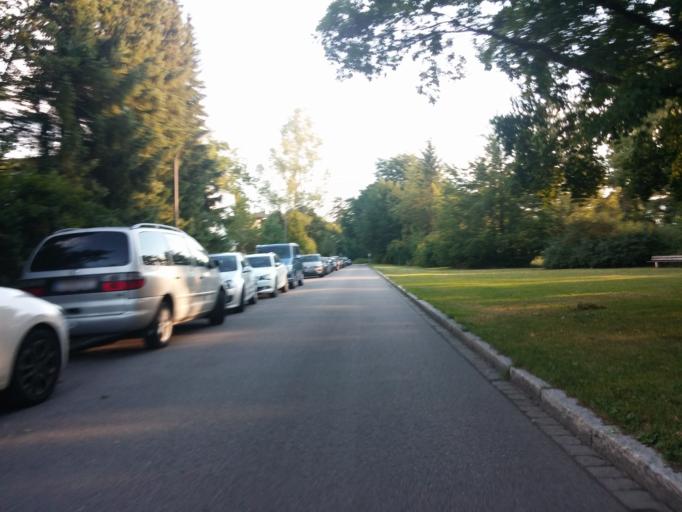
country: DE
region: Bavaria
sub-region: Upper Bavaria
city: Neubiberg
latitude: 48.1069
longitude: 11.6697
